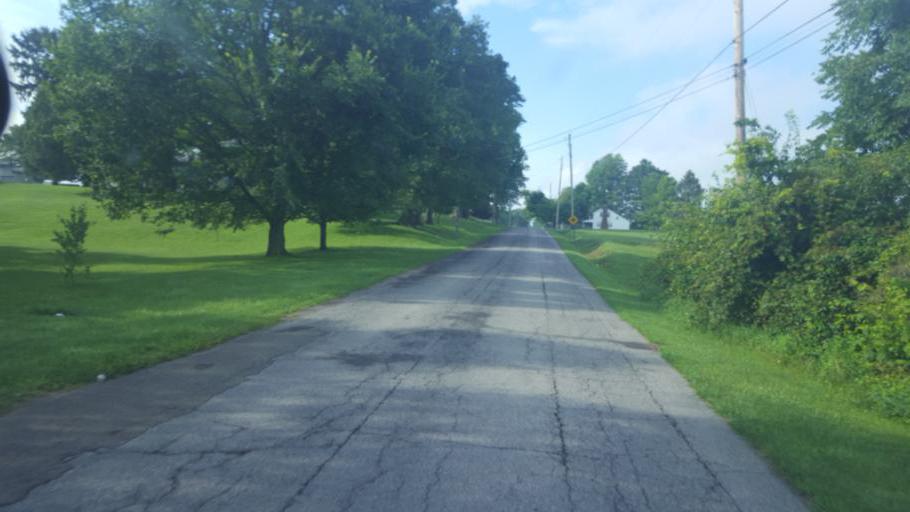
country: US
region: Ohio
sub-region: Morrow County
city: Mount Gilead
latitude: 40.5003
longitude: -82.8373
